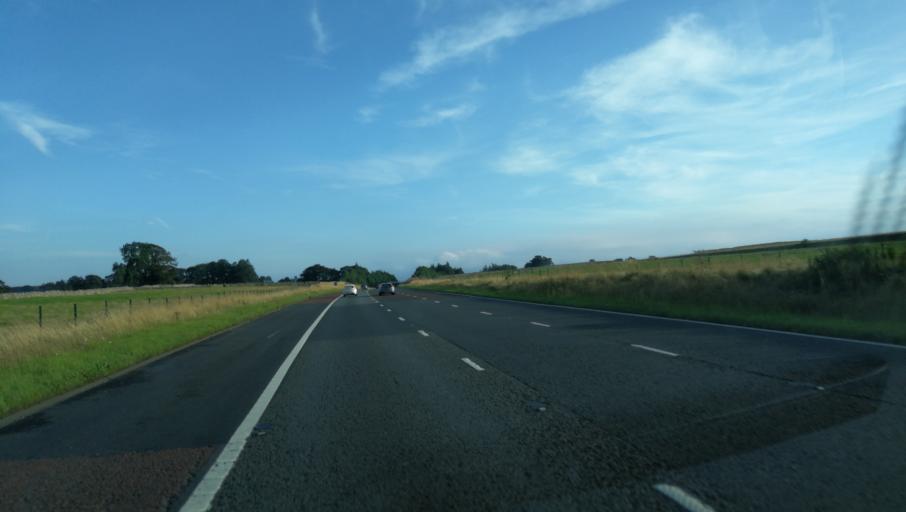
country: GB
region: England
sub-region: Cumbria
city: Penrith
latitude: 54.5382
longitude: -2.6595
